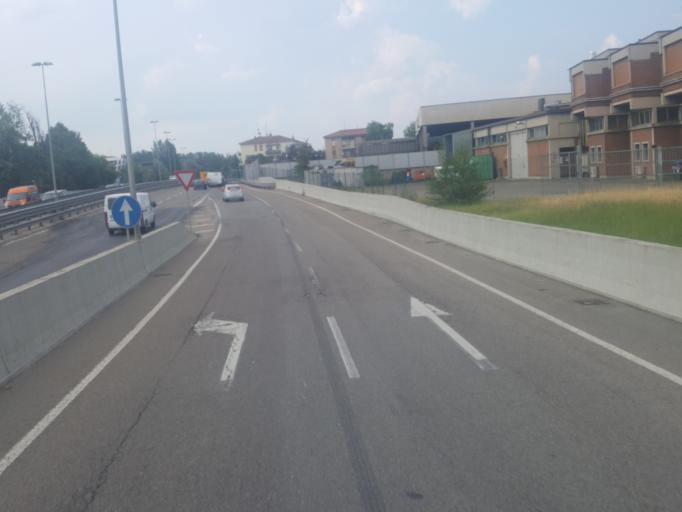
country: IT
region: Emilia-Romagna
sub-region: Provincia di Modena
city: Modena
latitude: 44.6339
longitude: 10.9578
